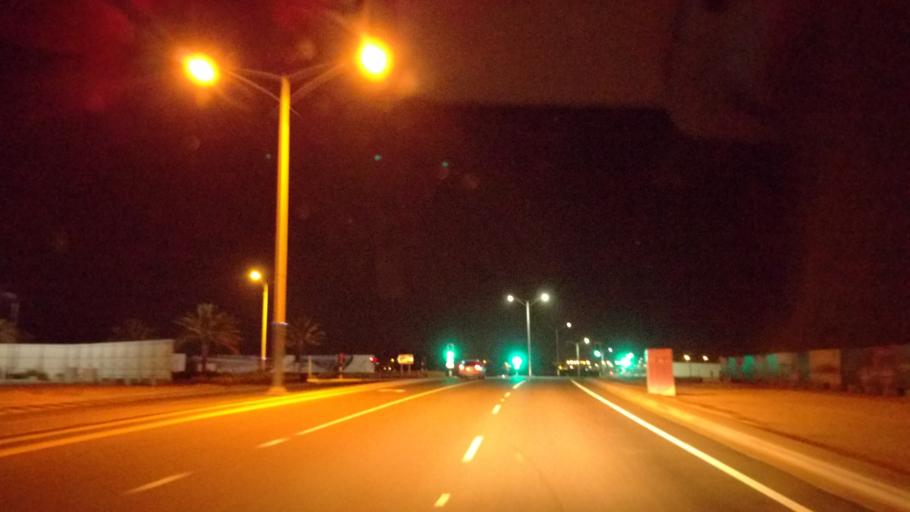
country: AE
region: Abu Dhabi
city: Abu Dhabi
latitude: 24.5407
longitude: 54.4421
